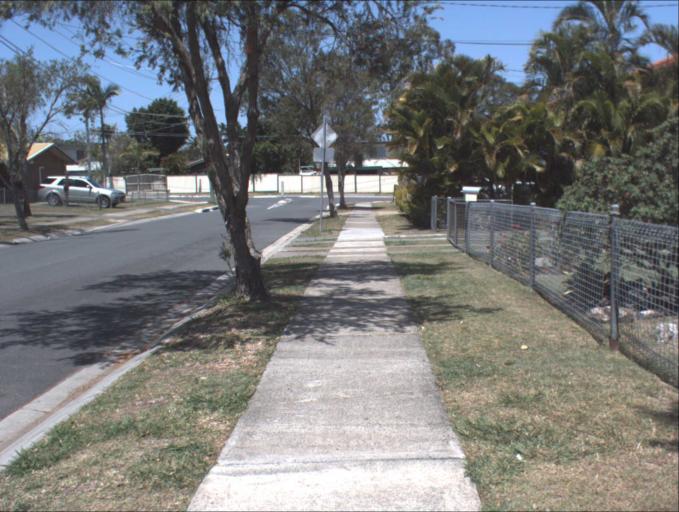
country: AU
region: Queensland
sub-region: Logan
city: Beenleigh
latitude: -27.6883
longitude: 153.1819
